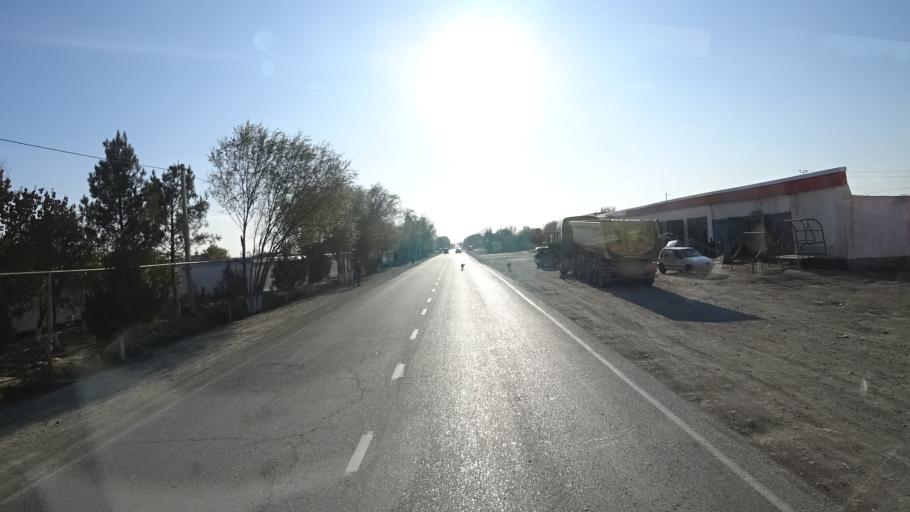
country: UZ
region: Navoiy
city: Beshrabot
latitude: 40.2007
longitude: 65.3772
